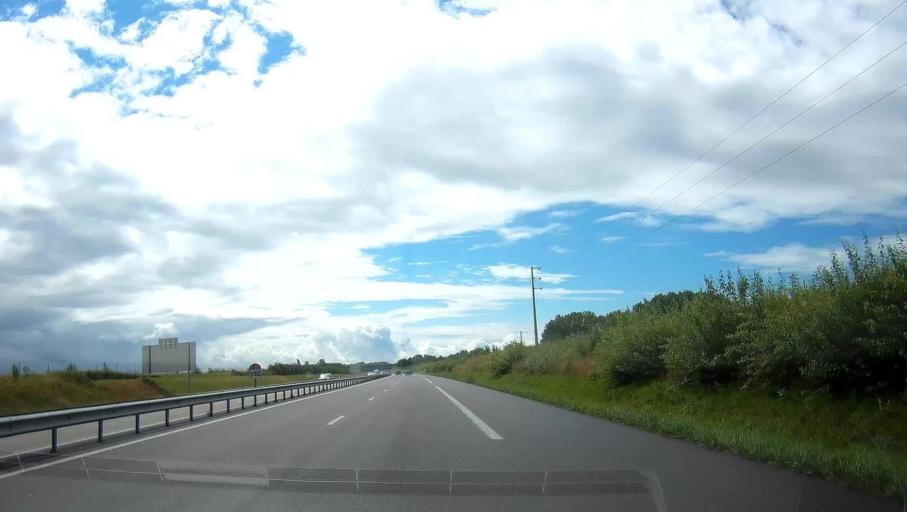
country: FR
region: Champagne-Ardenne
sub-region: Departement de l'Aube
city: Verrieres
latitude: 48.2481
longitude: 4.1683
